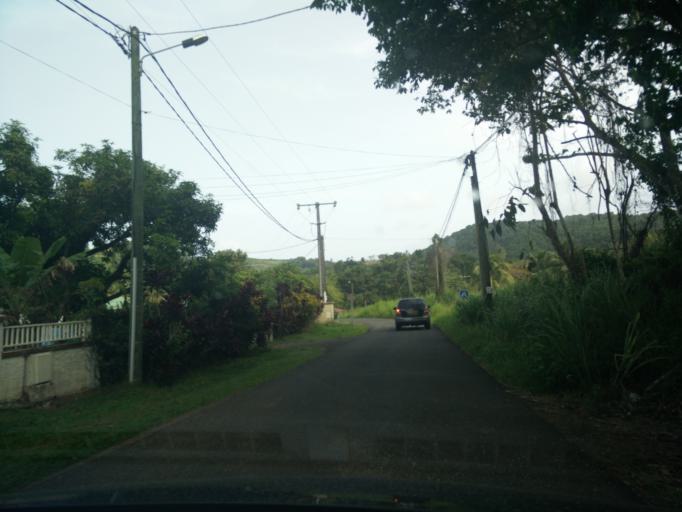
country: GP
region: Guadeloupe
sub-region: Guadeloupe
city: Petit-Bourg
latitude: 16.1197
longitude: -61.5949
